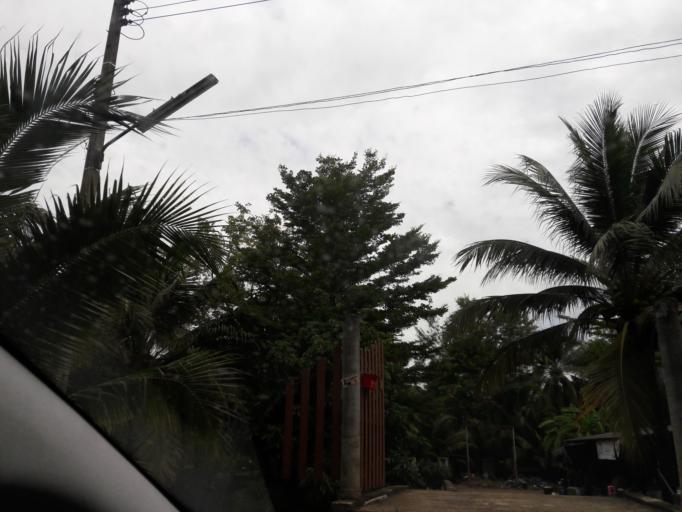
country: TH
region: Ratchaburi
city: Damnoen Saduak
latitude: 13.5337
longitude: 99.9488
